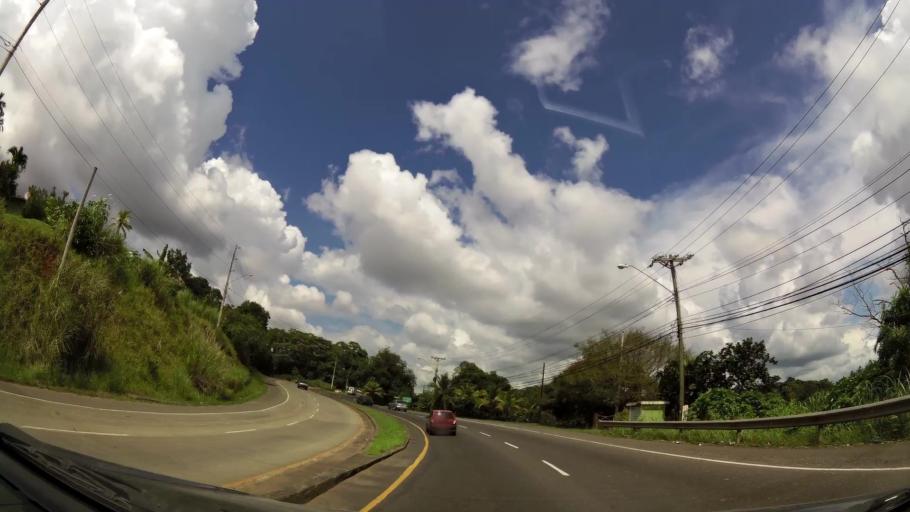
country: PA
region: Panama
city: Vista Alegre
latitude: 8.9422
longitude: -79.6794
